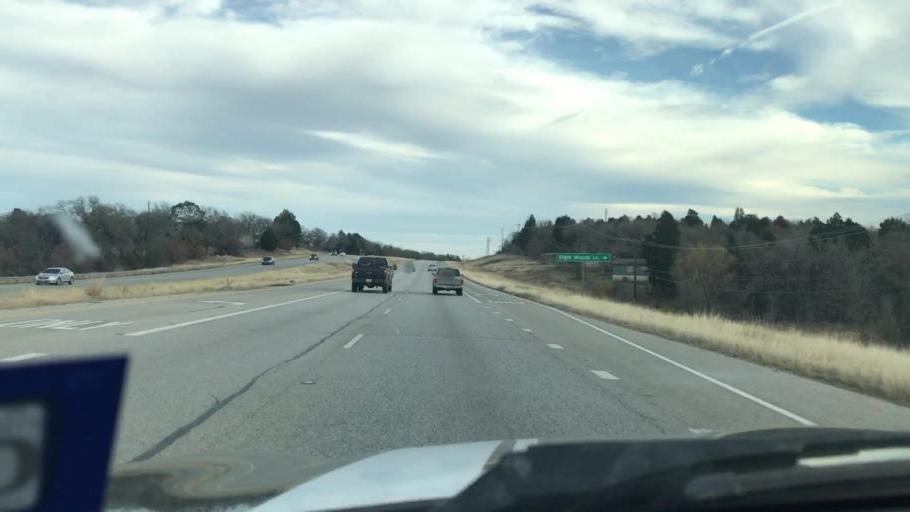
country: US
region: Texas
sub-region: Bastrop County
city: Elgin
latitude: 30.3266
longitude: -97.3331
